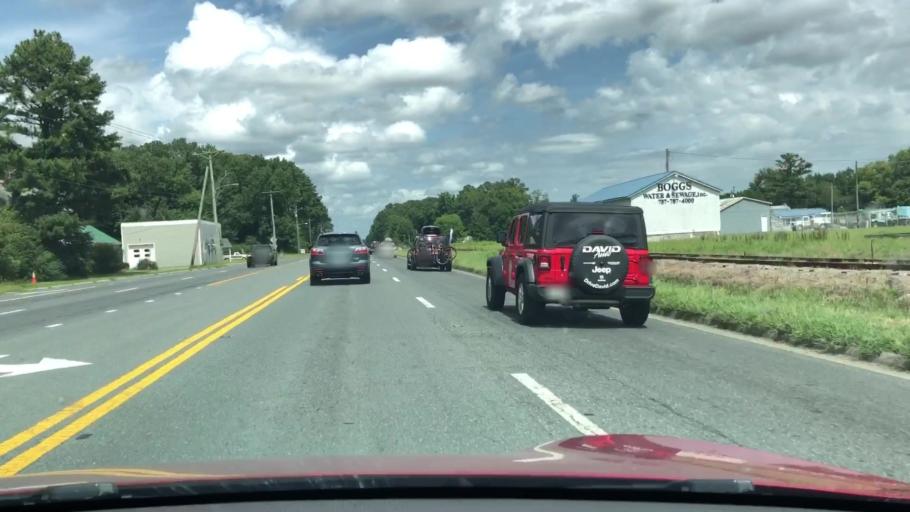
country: US
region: Virginia
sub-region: Accomack County
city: Onancock
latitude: 37.6507
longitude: -75.7419
